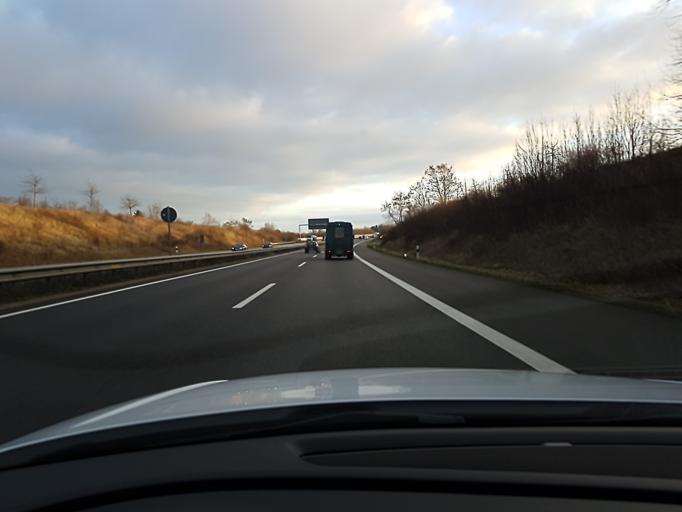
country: DE
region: Schleswig-Holstein
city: Hamberge
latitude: 53.8438
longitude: 10.6060
